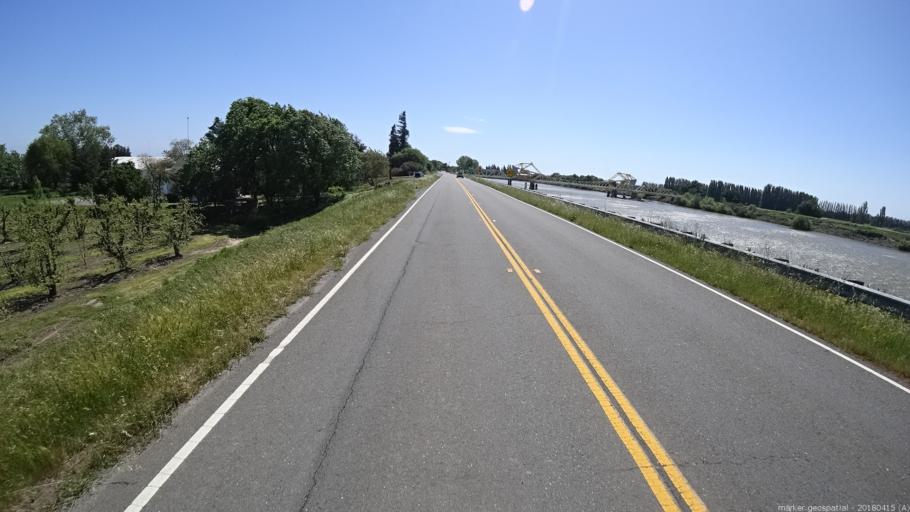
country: US
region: California
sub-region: Sacramento County
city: Walnut Grove
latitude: 38.3210
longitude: -121.5764
